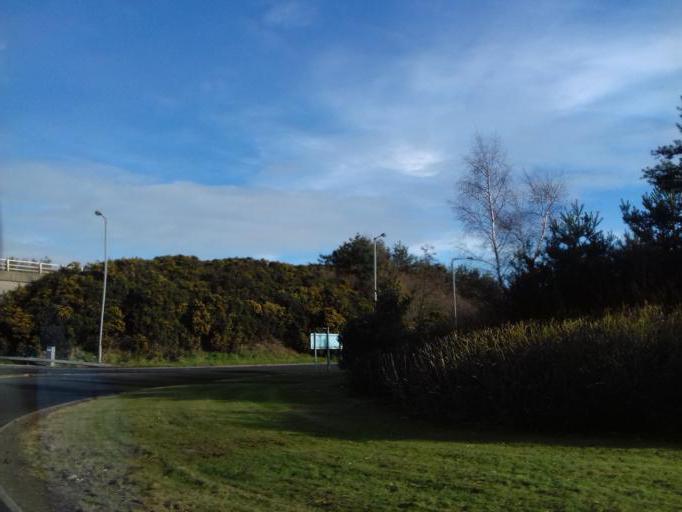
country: GB
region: Northern Ireland
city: Hillsborough
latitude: 54.4916
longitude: -6.0741
